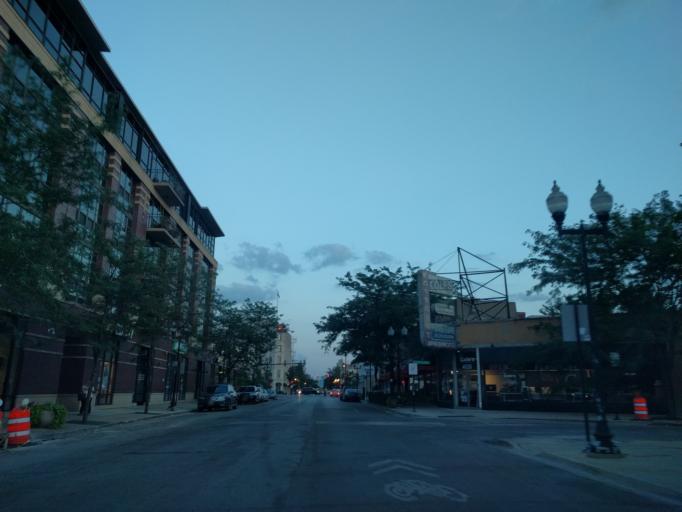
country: US
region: Illinois
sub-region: Cook County
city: Lincolnwood
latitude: 41.9553
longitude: -87.6796
